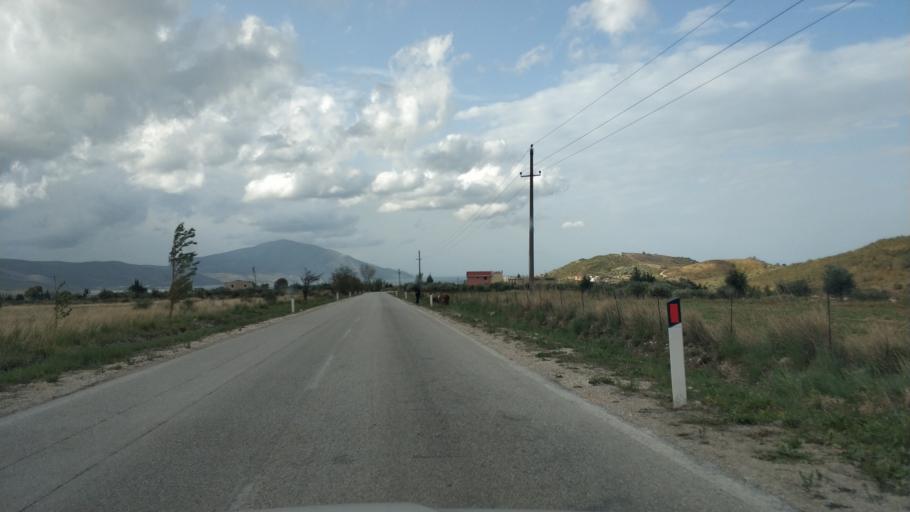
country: AL
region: Vlore
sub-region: Rrethi i Vlores
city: Orikum
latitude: 40.2868
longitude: 19.4954
